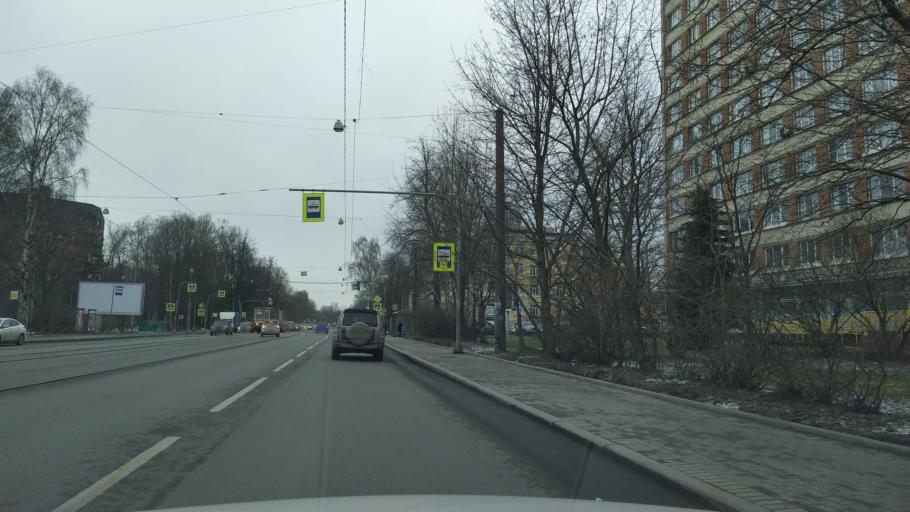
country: RU
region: Leningrad
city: Udel'naya
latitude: 60.0200
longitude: 30.3212
